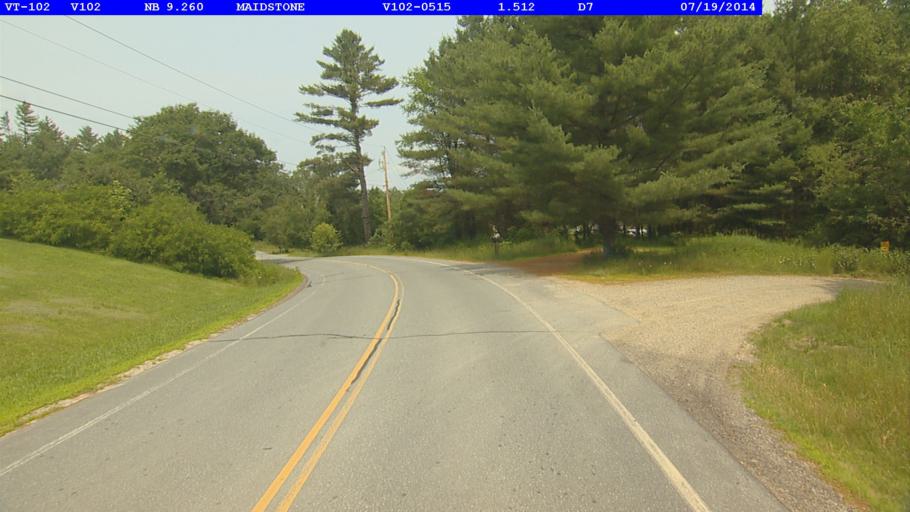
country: US
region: Vermont
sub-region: Essex County
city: Guildhall
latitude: 44.5899
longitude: -71.5490
